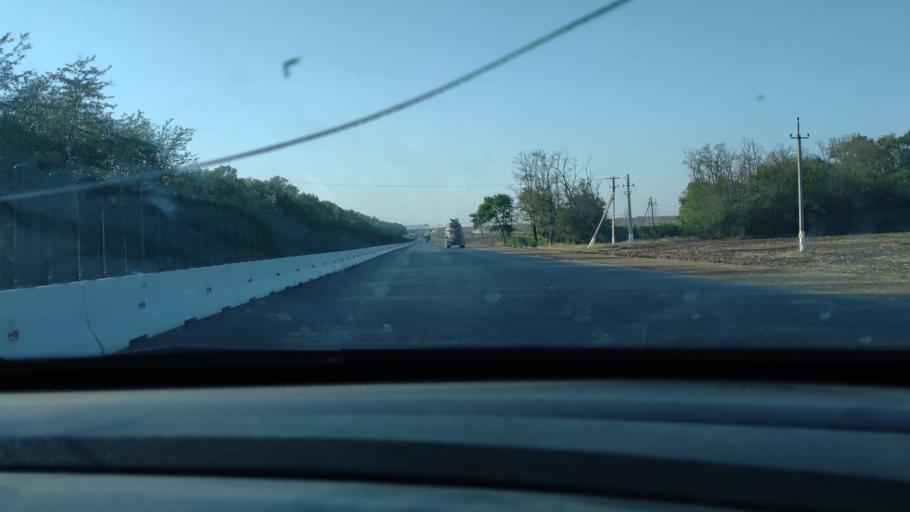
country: RU
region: Krasnodarskiy
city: Medvedovskaya
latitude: 45.4816
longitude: 38.9667
